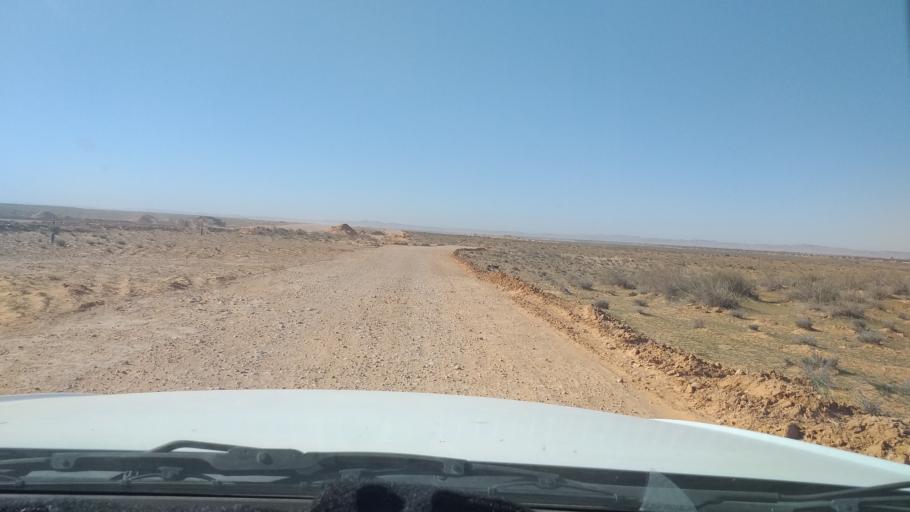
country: TN
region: Madanin
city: Medenine
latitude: 33.2645
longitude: 10.5802
